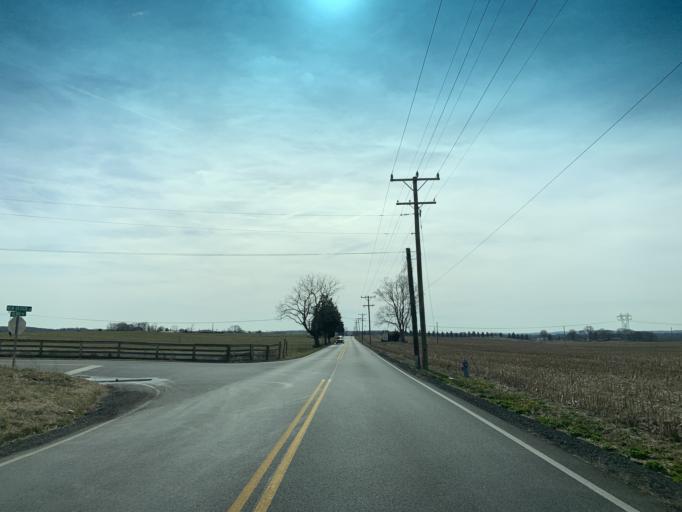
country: US
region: Maryland
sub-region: Frederick County
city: Adamstown
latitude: 39.2954
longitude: -77.4660
